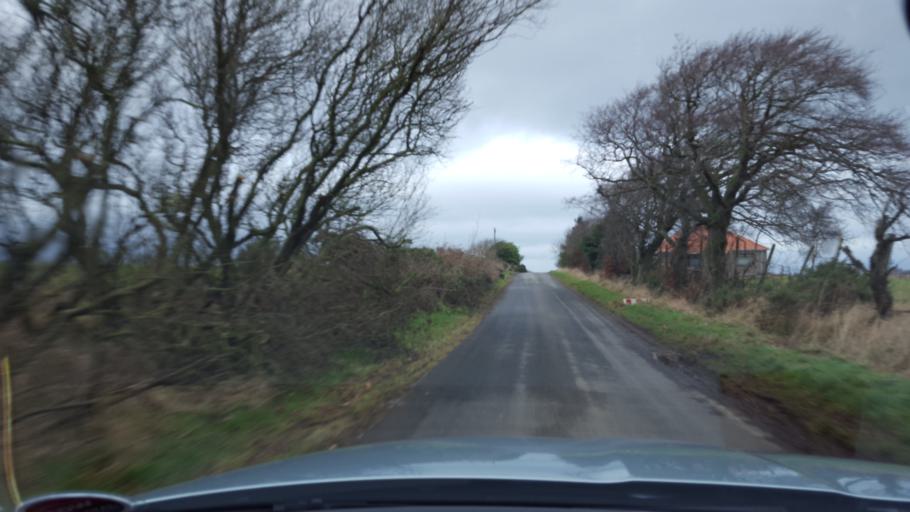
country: GB
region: Scotland
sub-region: West Lothian
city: Kirknewton
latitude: 55.8628
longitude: -3.4296
